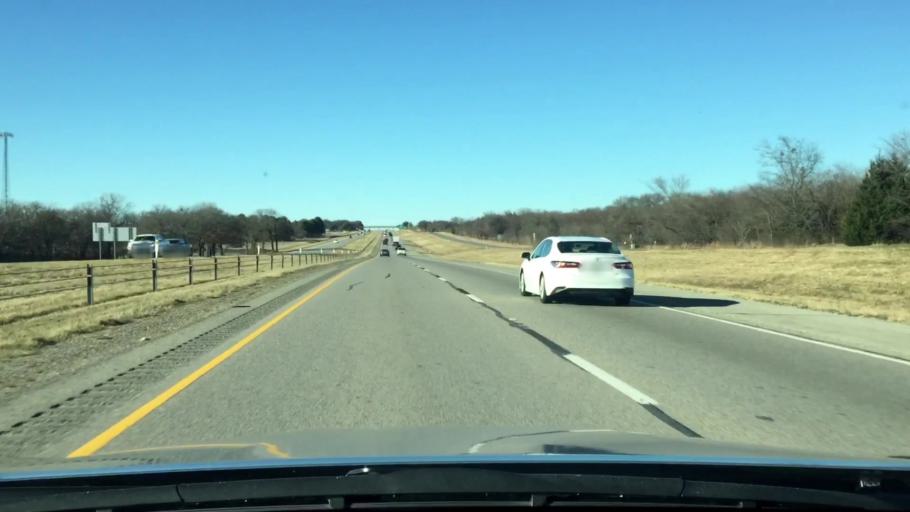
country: US
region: Texas
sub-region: Johnson County
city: Alvarado
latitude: 32.3692
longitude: -97.2018
